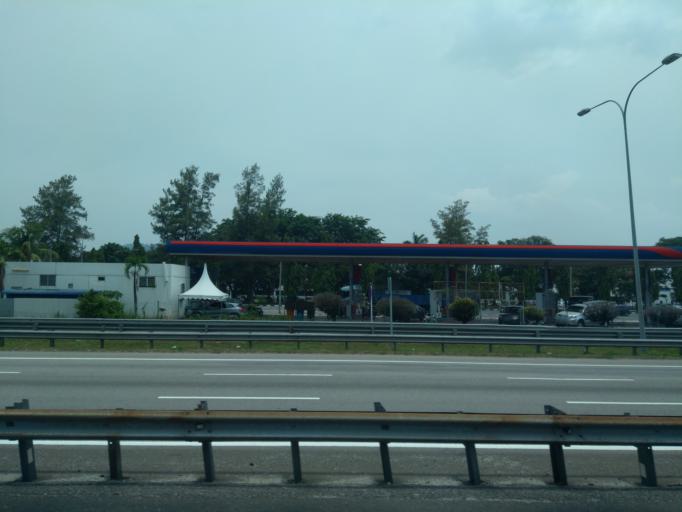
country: MY
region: Penang
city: Perai
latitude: 5.3559
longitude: 100.4150
